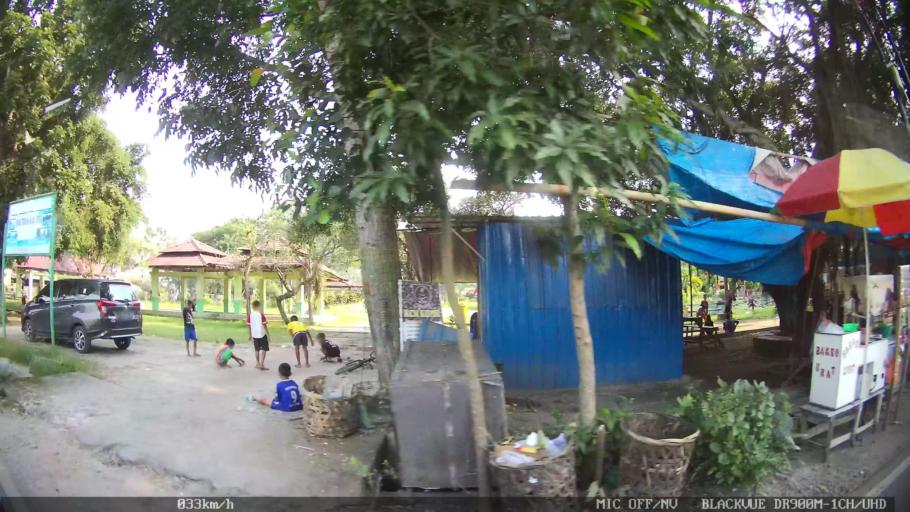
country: ID
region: North Sumatra
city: Binjai
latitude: 3.6029
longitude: 98.4993
